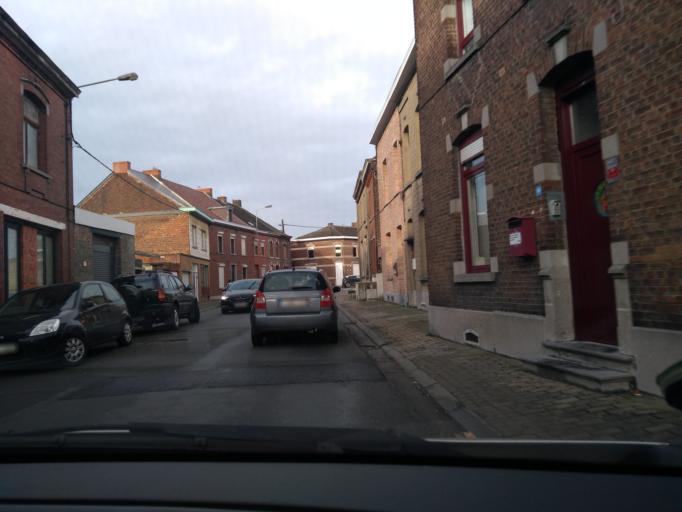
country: BE
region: Wallonia
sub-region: Province du Hainaut
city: Colfontaine
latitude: 50.4095
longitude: 3.8684
